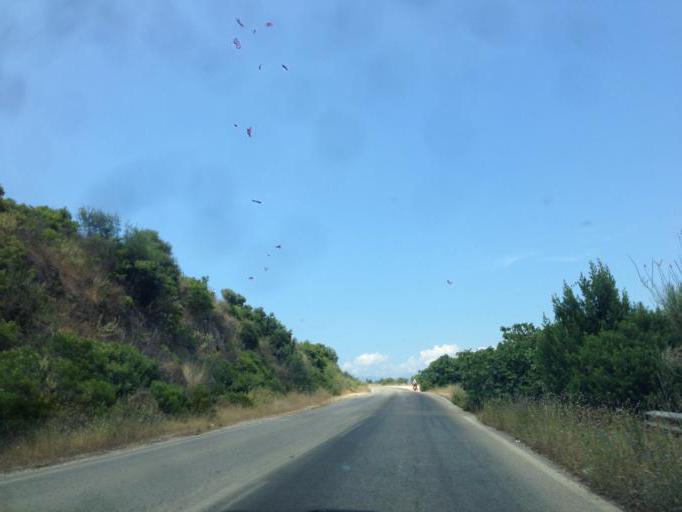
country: GR
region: Ionian Islands
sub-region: Nomos Kerkyras
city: Acharavi
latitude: 39.7923
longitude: 19.9029
